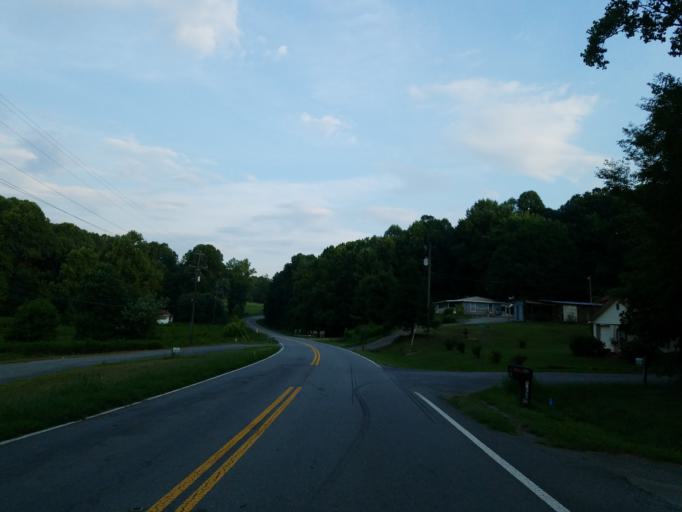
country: US
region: Georgia
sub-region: Gilmer County
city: Ellijay
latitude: 34.6353
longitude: -84.4703
